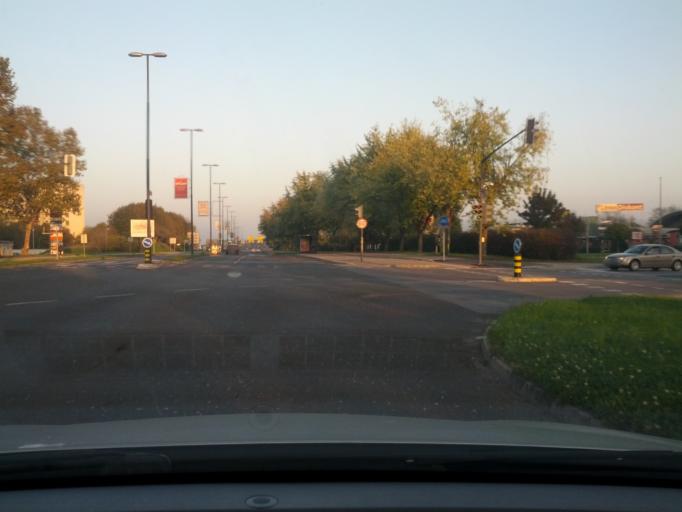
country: SI
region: Ljubljana
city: Ljubljana
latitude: 46.0698
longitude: 14.5457
